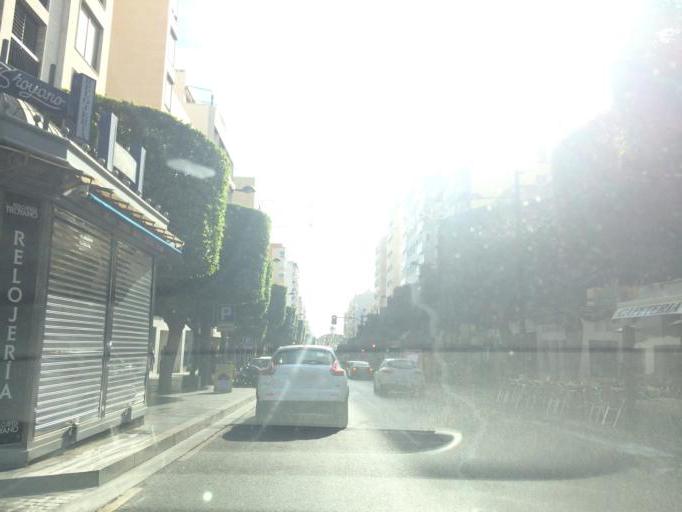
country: ES
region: Andalusia
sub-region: Provincia de Almeria
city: Almeria
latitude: 36.8410
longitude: -2.4638
